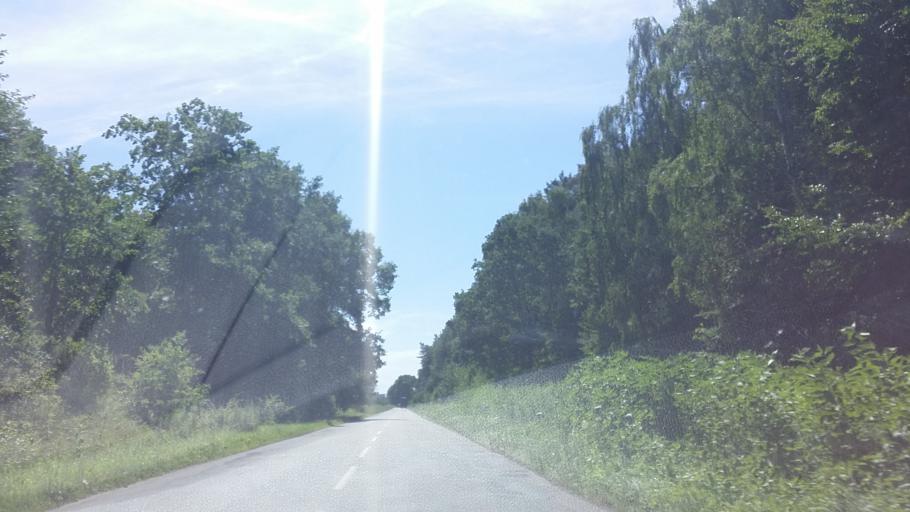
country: PL
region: West Pomeranian Voivodeship
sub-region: Powiat lobeski
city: Lobez
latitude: 53.6608
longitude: 15.6504
